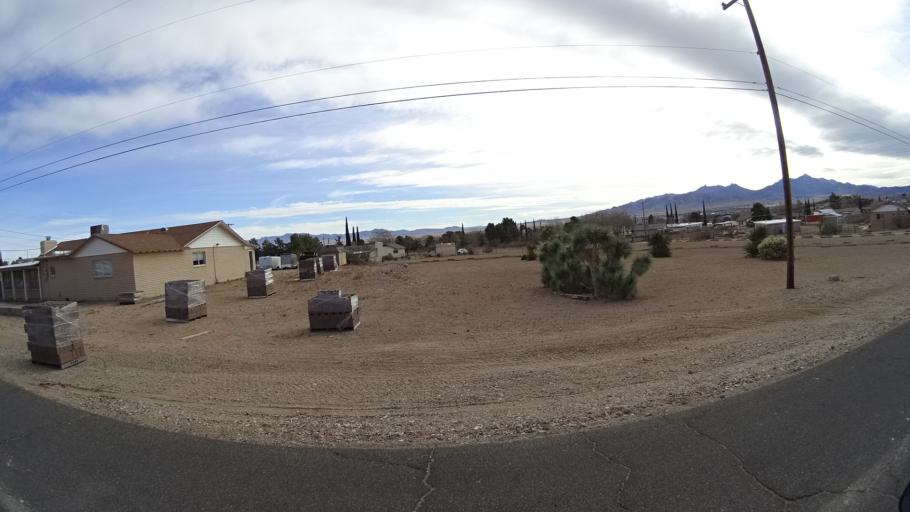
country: US
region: Arizona
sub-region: Mohave County
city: New Kingman-Butler
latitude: 35.2326
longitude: -114.0493
